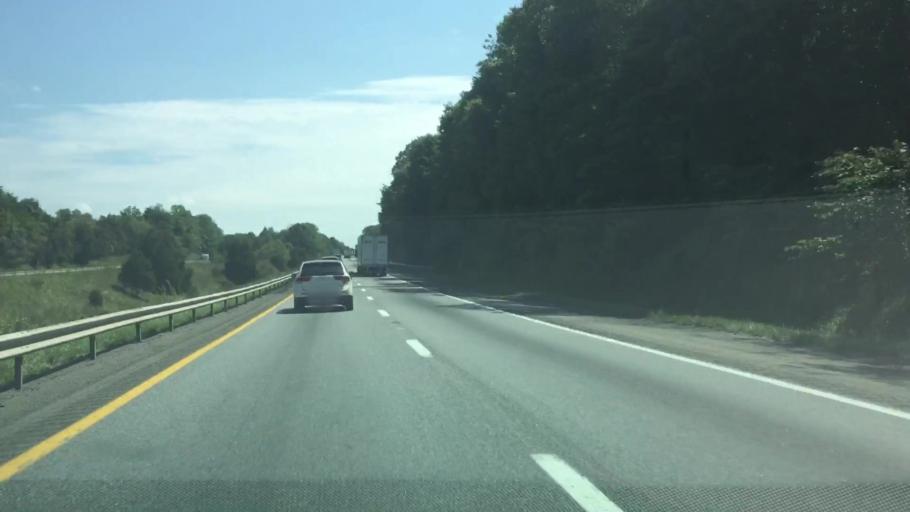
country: US
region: Virginia
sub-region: City of Radford
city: Radford
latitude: 37.0994
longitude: -80.5511
